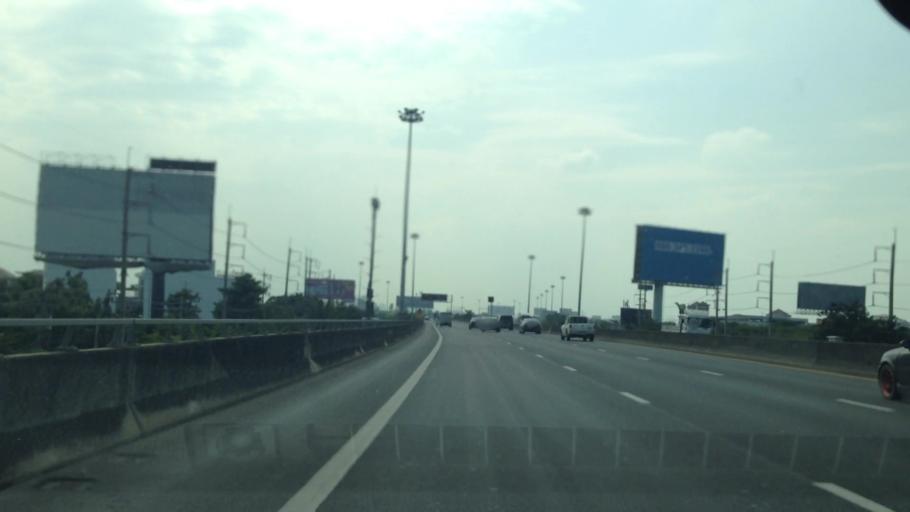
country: TH
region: Bangkok
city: Lat Phrao
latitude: 13.8320
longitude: 100.6291
